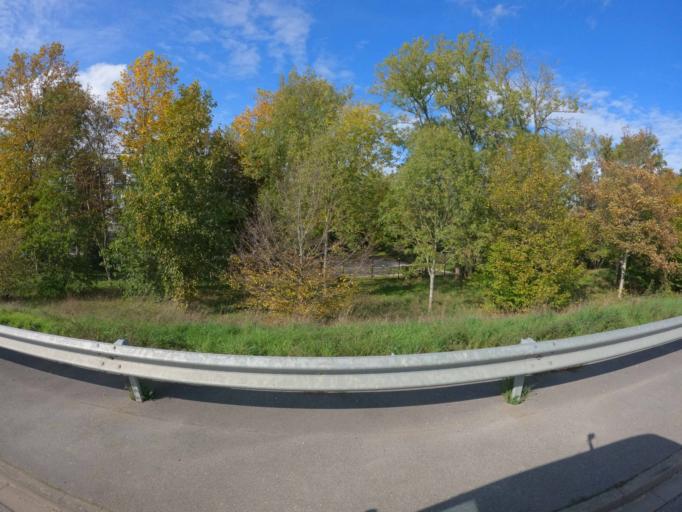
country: FR
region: Ile-de-France
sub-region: Departement de Seine-et-Marne
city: Vaires-sur-Marne
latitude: 48.8749
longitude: 2.6478
